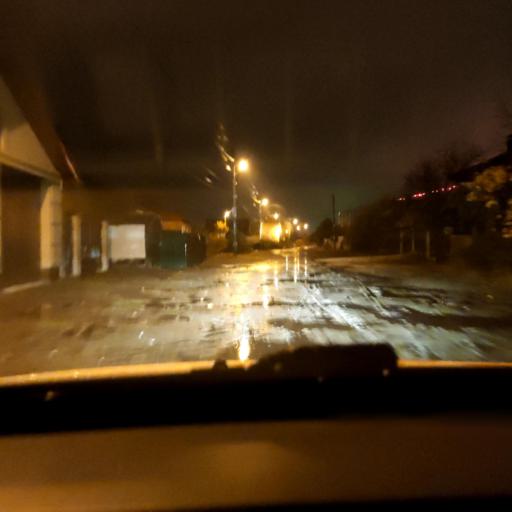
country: RU
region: Voronezj
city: Somovo
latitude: 51.7406
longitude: 39.3227
